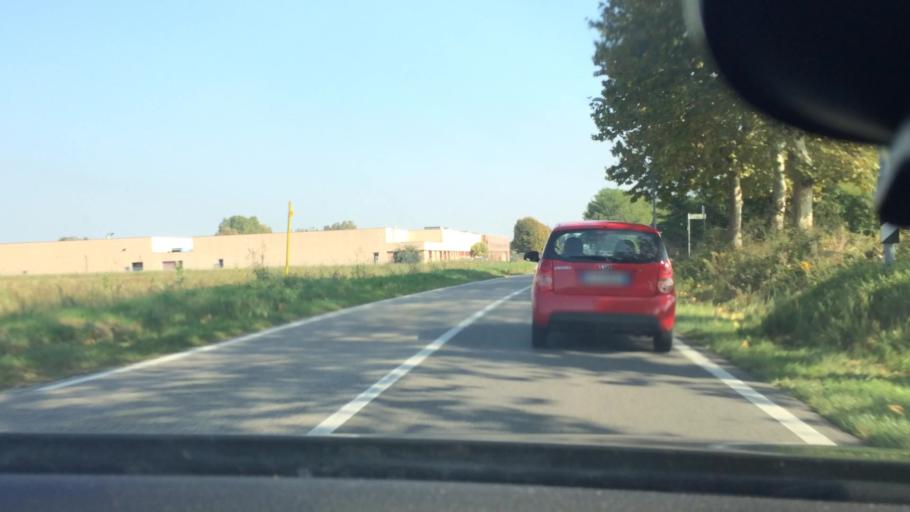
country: IT
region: Lombardy
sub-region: Citta metropolitana di Milano
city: Santo Stefano Ticino
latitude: 45.4914
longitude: 8.9024
